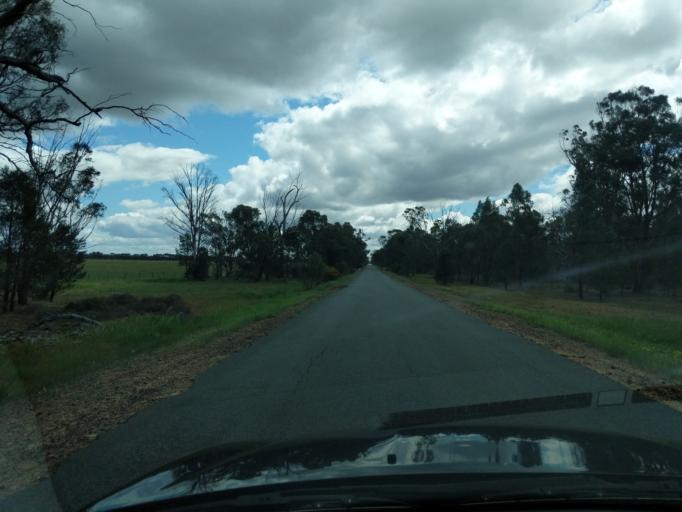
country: AU
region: New South Wales
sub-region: Coolamon
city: Coolamon
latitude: -34.9393
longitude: 146.9706
